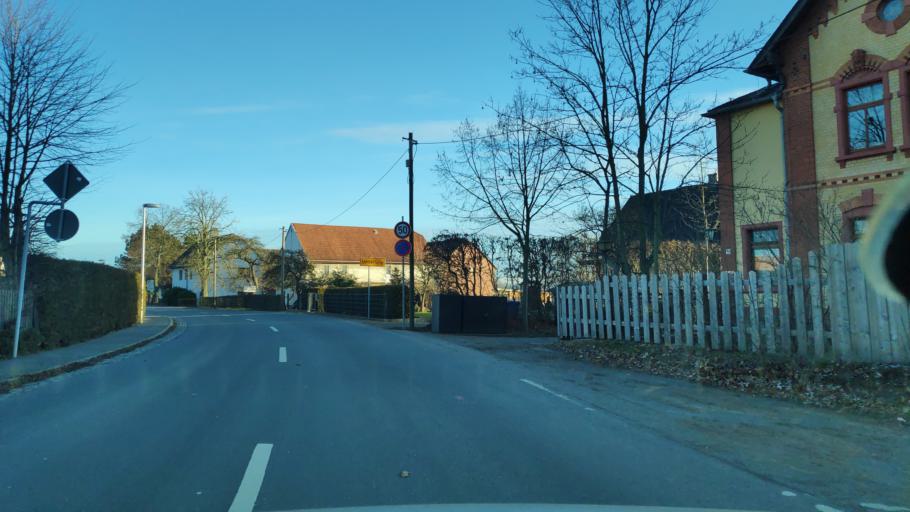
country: DE
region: Thuringia
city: Thonhausen
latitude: 50.8052
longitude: 12.3090
